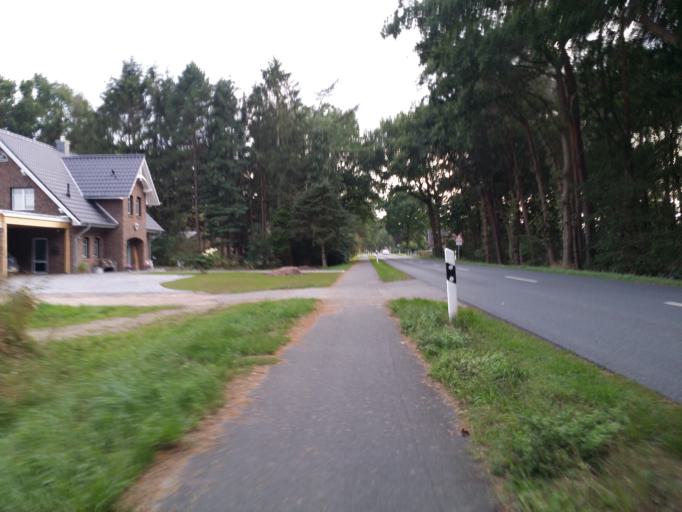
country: DE
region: Lower Saxony
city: Sandbostel
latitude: 53.4470
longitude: 9.1058
